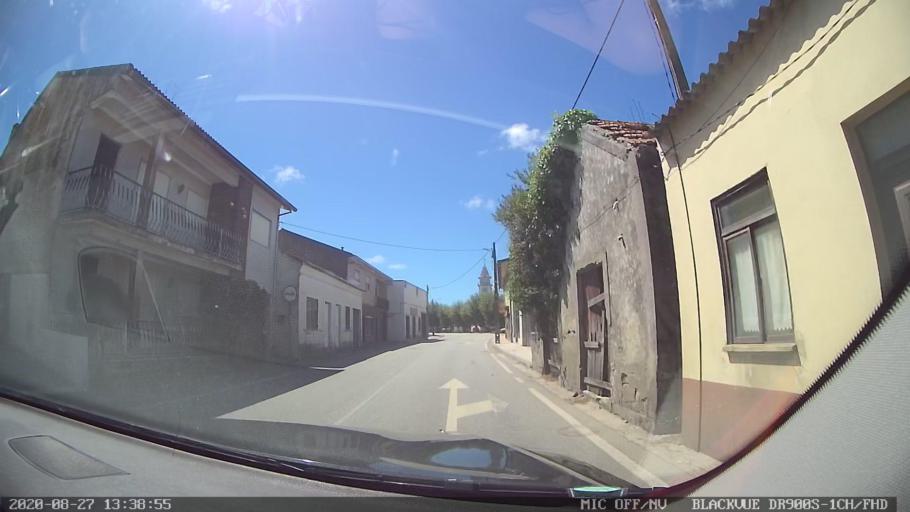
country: PT
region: Coimbra
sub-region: Mira
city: Mira
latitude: 40.4441
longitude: -8.7278
